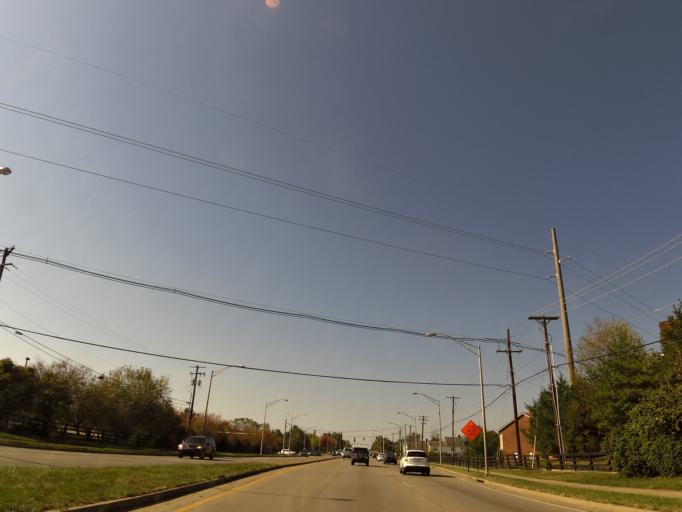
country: US
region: Kentucky
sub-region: Fayette County
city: Lexington-Fayette
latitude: 38.0080
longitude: -84.4246
